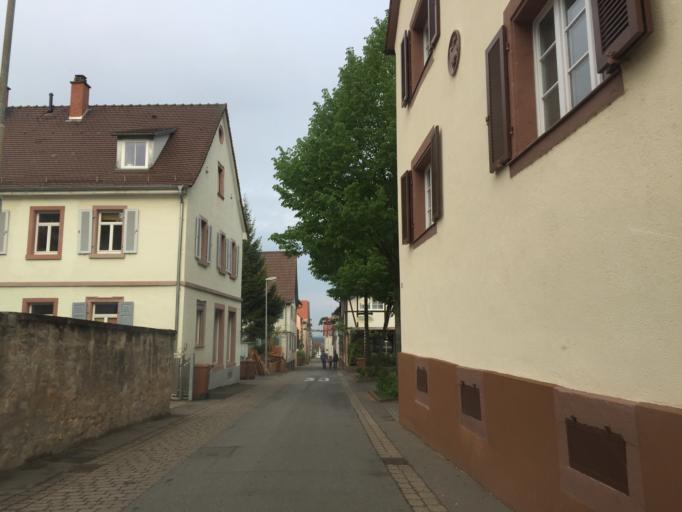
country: DE
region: Baden-Wuerttemberg
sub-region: Karlsruhe Region
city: Weinheim
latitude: 49.5254
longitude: 8.6664
